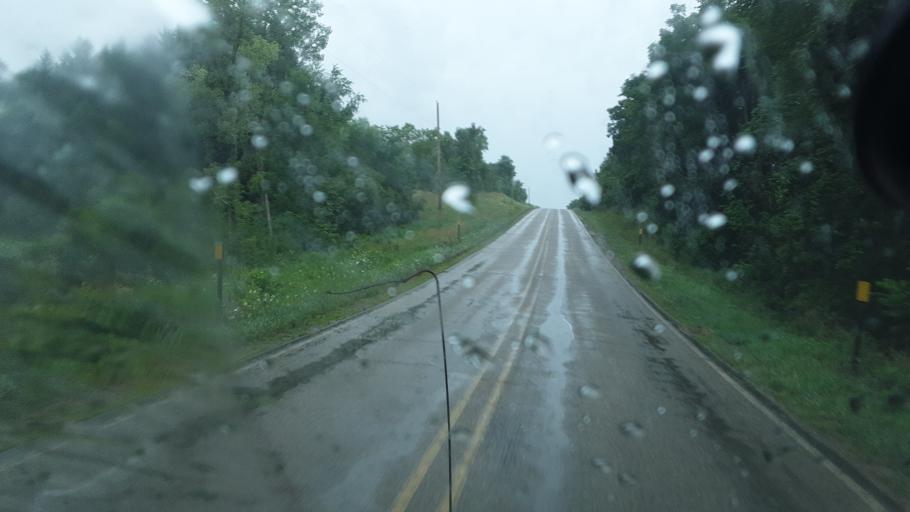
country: US
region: Ohio
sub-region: Williams County
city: Pioneer
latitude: 41.7088
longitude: -84.6634
